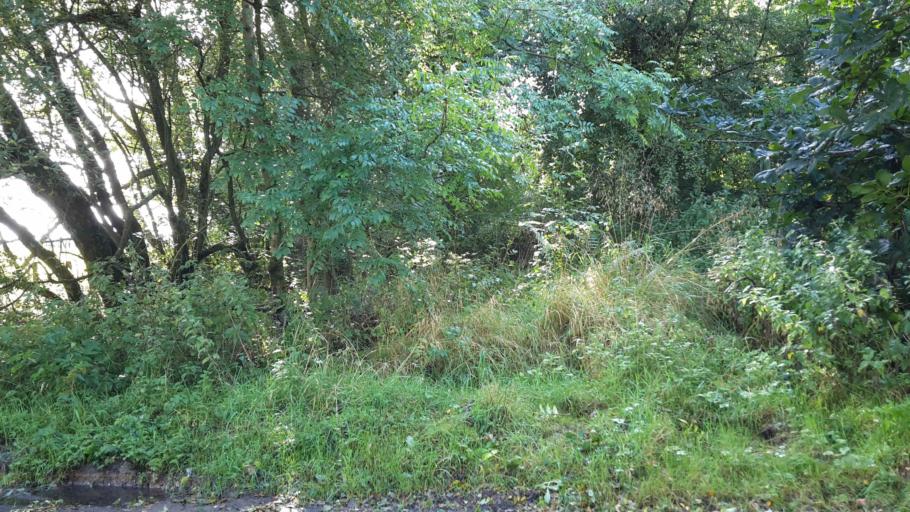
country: GB
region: Scotland
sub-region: South Lanarkshire
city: Law
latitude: 55.7253
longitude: -3.8652
